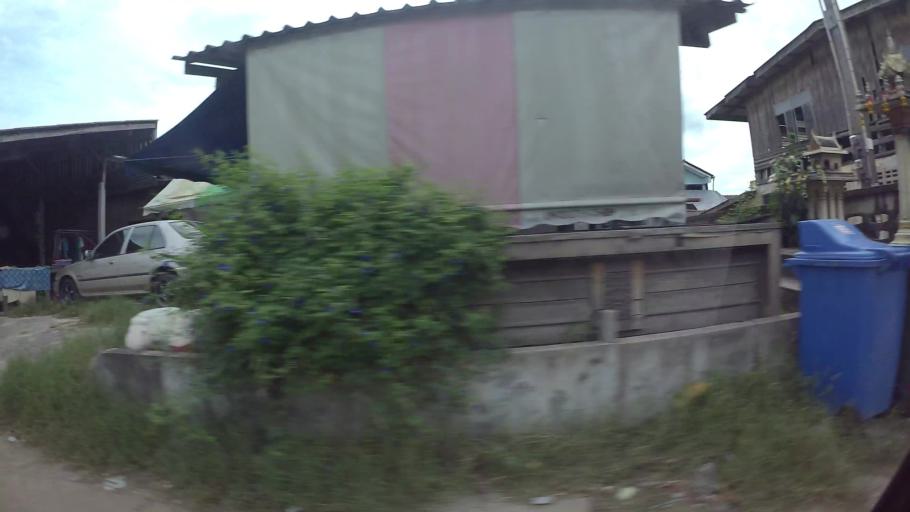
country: TH
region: Chon Buri
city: Si Racha
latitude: 13.1271
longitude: 100.9707
